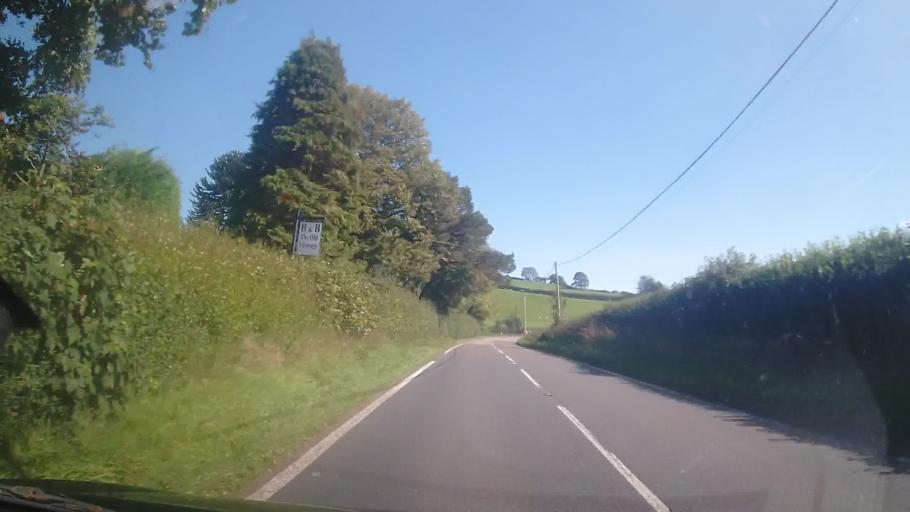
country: GB
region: Wales
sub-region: Sir Powys
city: Mochdre
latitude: 52.4797
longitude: -3.3269
